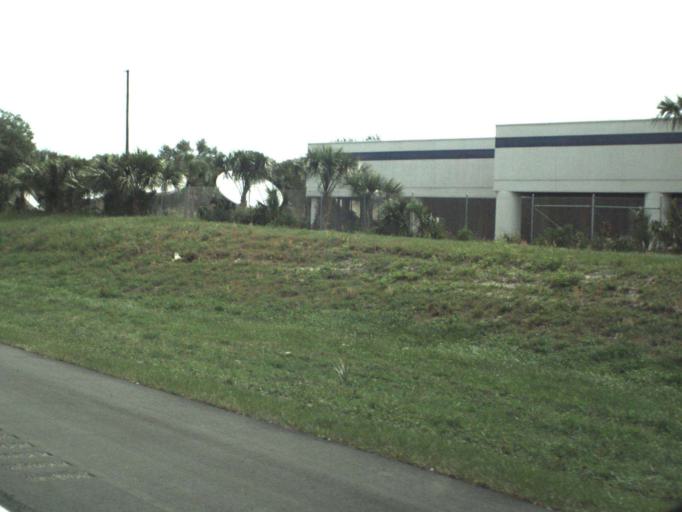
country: US
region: Florida
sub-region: Seminole County
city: Heathrow
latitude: 28.7392
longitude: -81.3692
